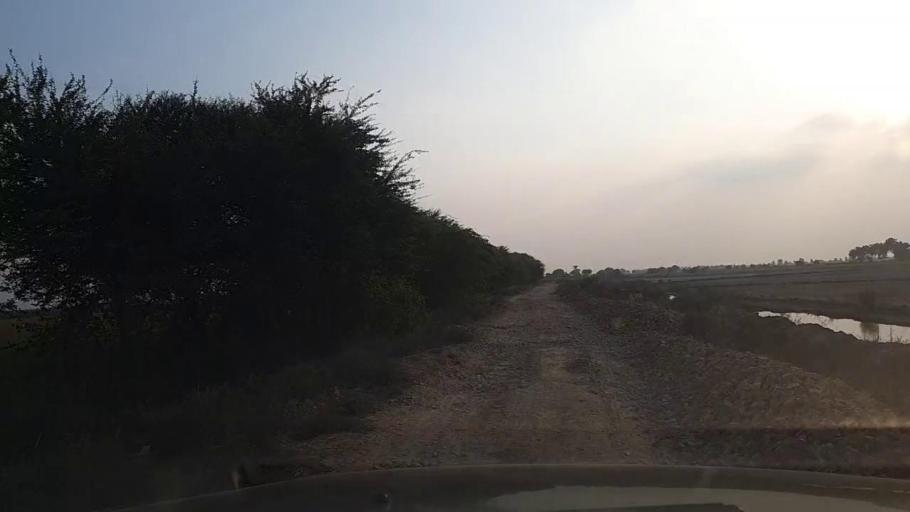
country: PK
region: Sindh
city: Jati
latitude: 24.5371
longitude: 68.3607
